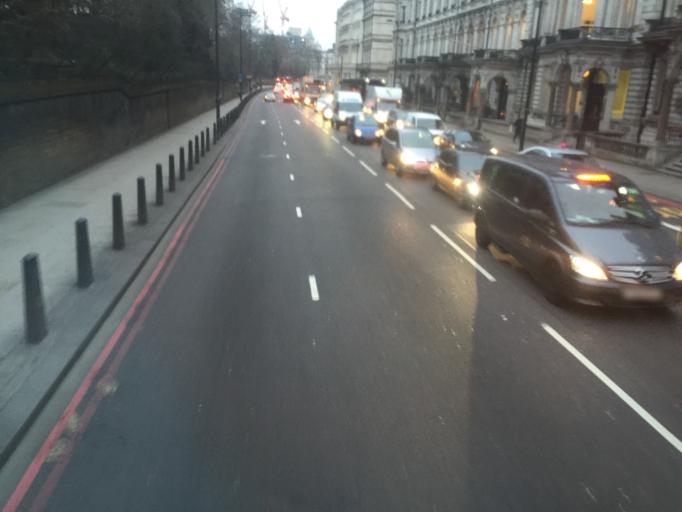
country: GB
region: England
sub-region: Greater London
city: Chelsea
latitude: 51.5014
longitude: -0.1508
